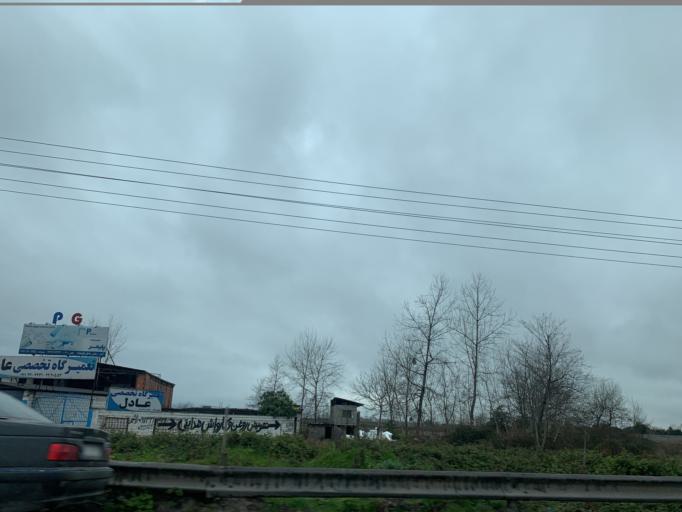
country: IR
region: Mazandaran
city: Amol
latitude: 36.4189
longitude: 52.3493
